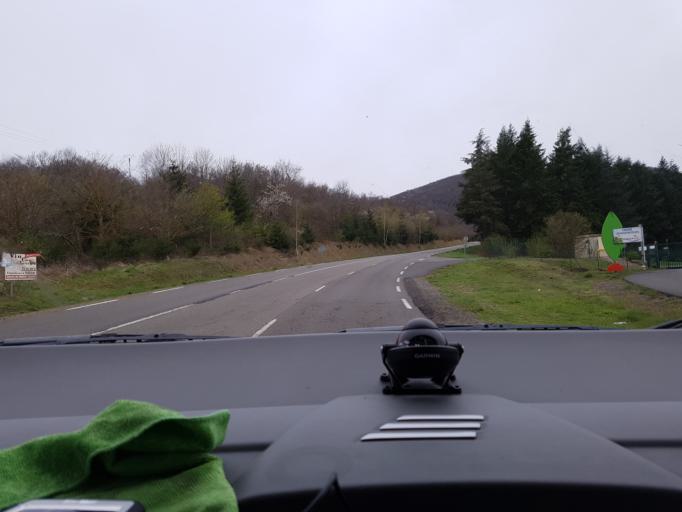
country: FR
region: Auvergne
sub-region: Departement du Puy-de-Dome
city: Enval
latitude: 45.8821
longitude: 3.0556
